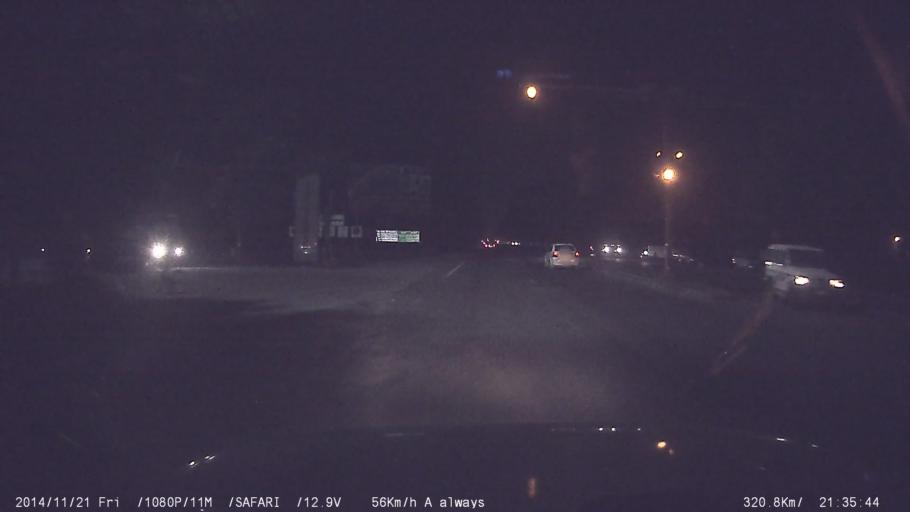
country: IN
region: Tamil Nadu
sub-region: Kancheepuram
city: Singapperumalkovil
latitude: 12.7429
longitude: 79.9923
